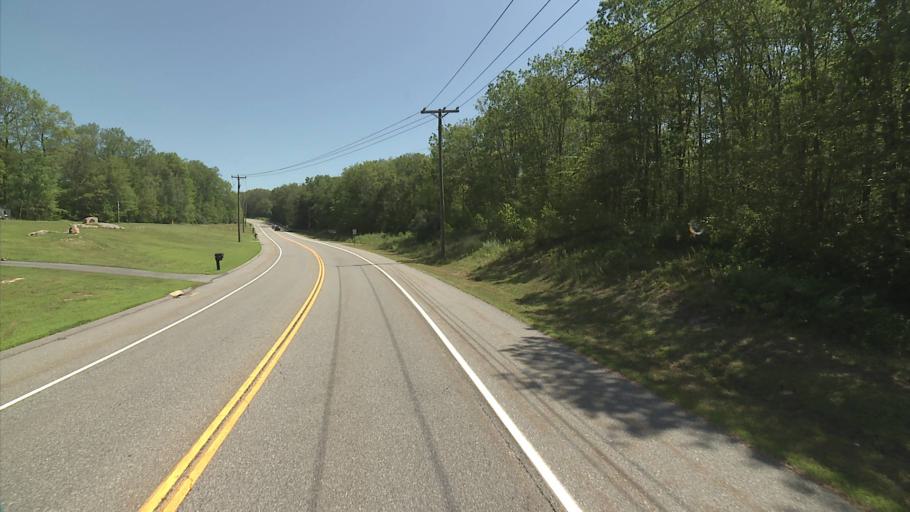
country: US
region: Connecticut
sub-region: Windham County
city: Moosup
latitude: 41.6822
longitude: -71.8613
